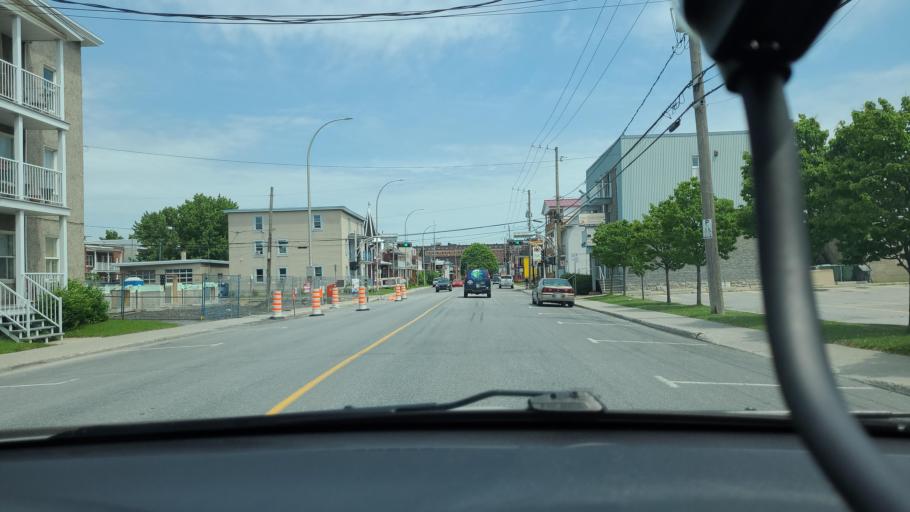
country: CA
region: Quebec
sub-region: Monteregie
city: Saint-Hyacinthe
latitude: 45.6230
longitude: -72.9549
